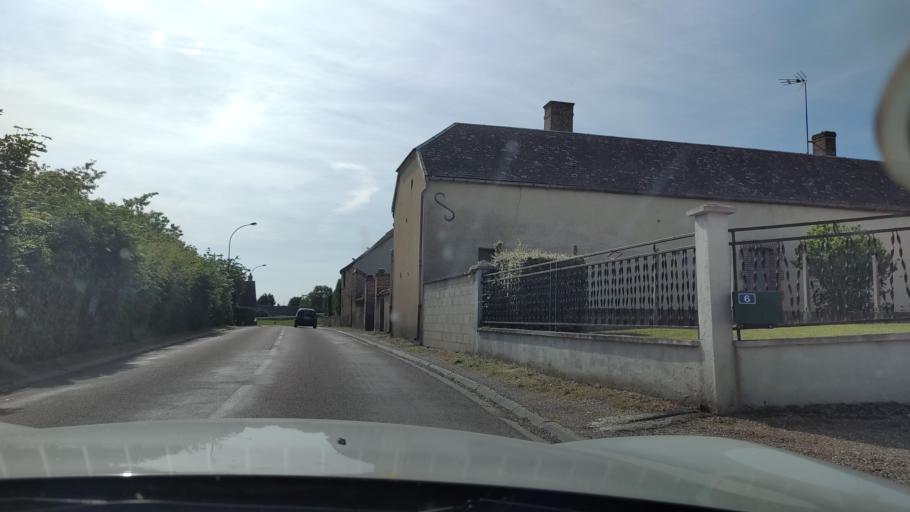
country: FR
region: Champagne-Ardenne
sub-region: Departement de l'Aube
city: Nogent-sur-Seine
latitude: 48.4488
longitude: 3.6113
